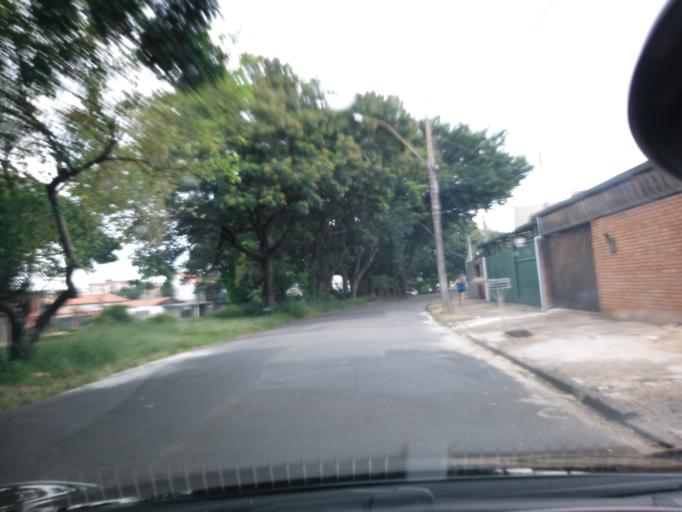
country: BR
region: Sao Paulo
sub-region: Campinas
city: Campinas
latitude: -22.8779
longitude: -47.0373
